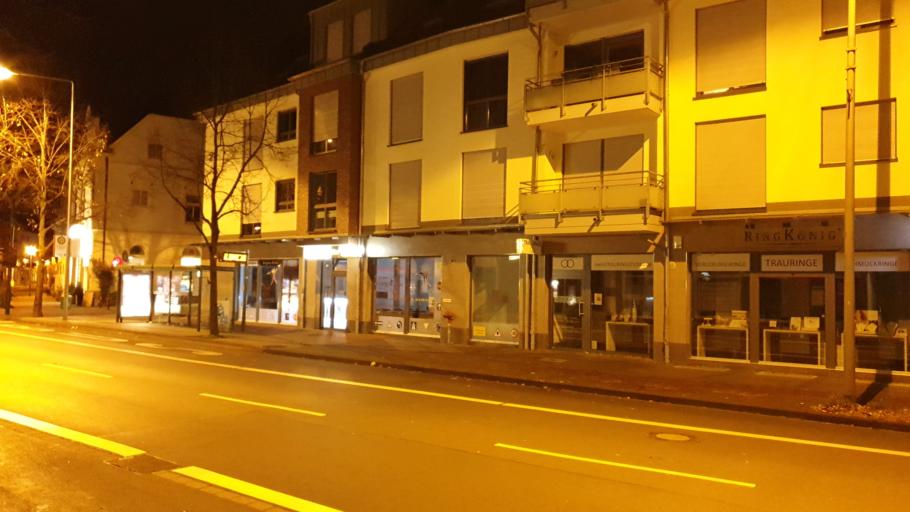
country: DE
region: North Rhine-Westphalia
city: Opladen
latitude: 51.0332
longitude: 7.0478
